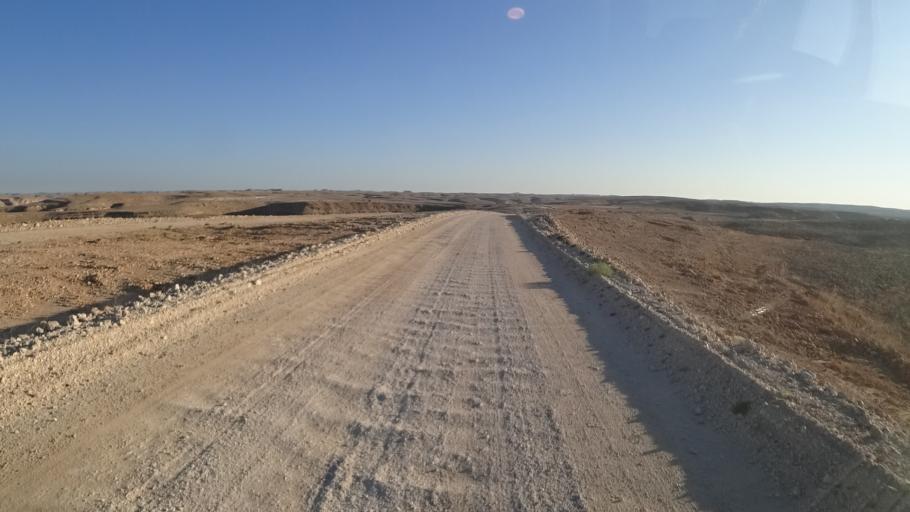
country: YE
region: Al Mahrah
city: Hawf
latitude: 17.1934
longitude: 53.3390
